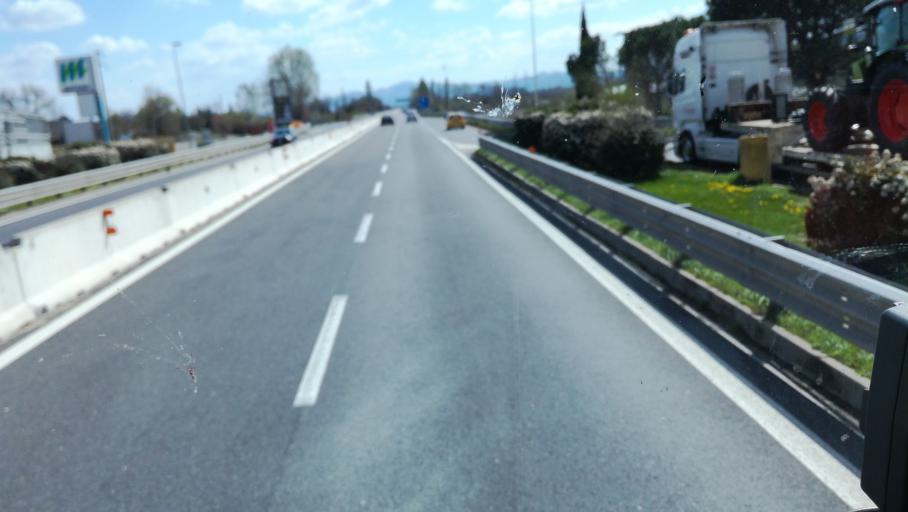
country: IT
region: Tuscany
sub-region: Province of Arezzo
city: Santa Fiora
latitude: 43.5765
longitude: 12.1175
